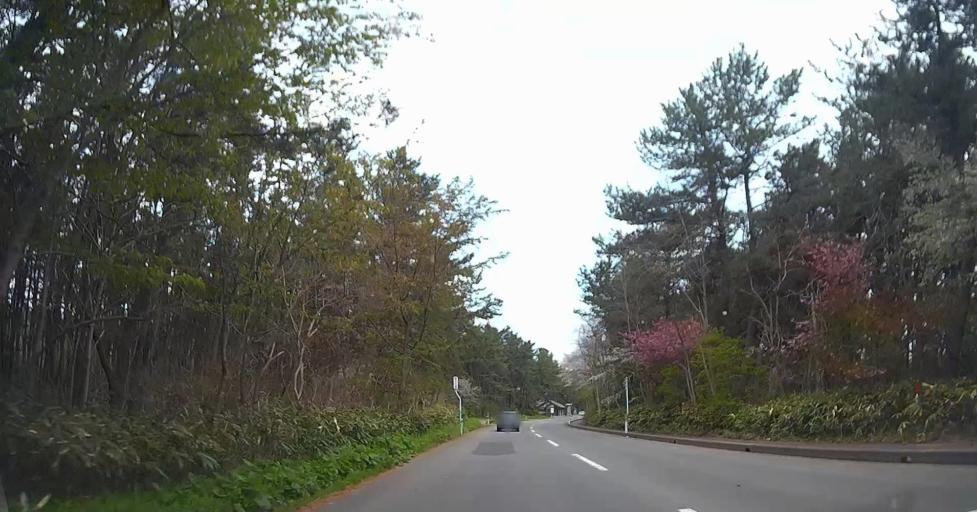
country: JP
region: Aomori
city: Shimokizukuri
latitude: 41.0148
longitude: 140.3339
